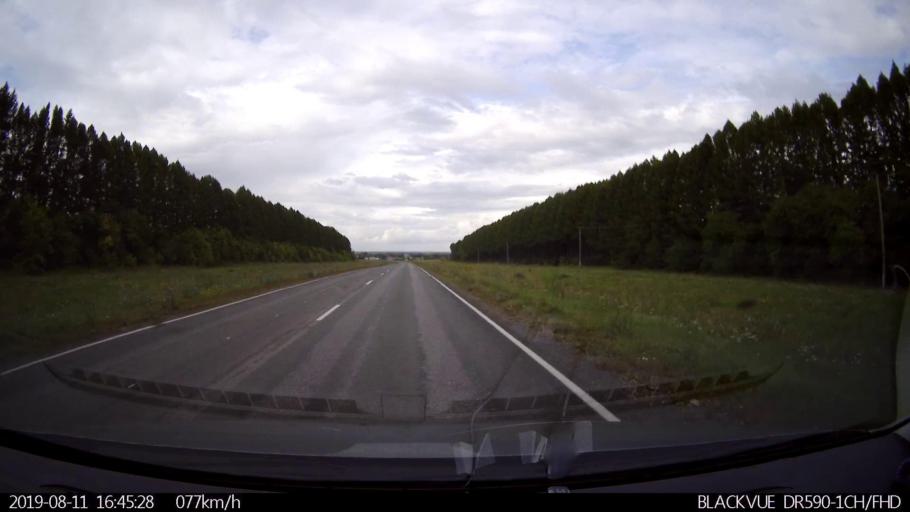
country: RU
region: Ulyanovsk
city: Mayna
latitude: 54.1900
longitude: 47.6861
